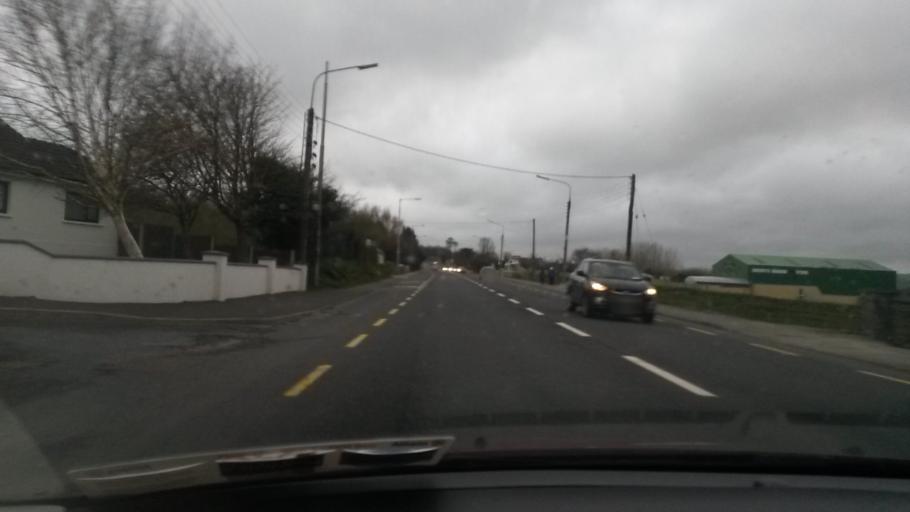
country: IE
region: Munster
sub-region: County Limerick
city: Abbeyfeale
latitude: 52.3783
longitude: -9.3055
